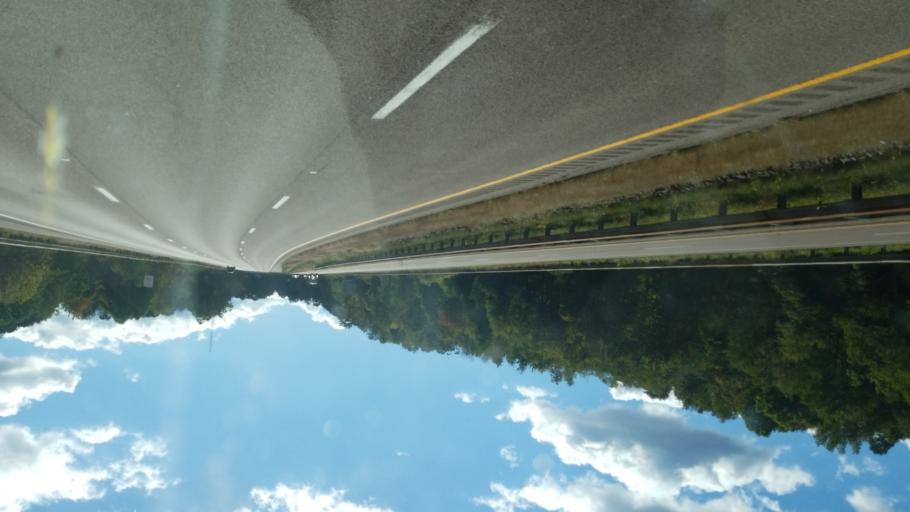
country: US
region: West Virginia
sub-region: Preston County
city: Terra Alta
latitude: 39.6599
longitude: -79.4303
